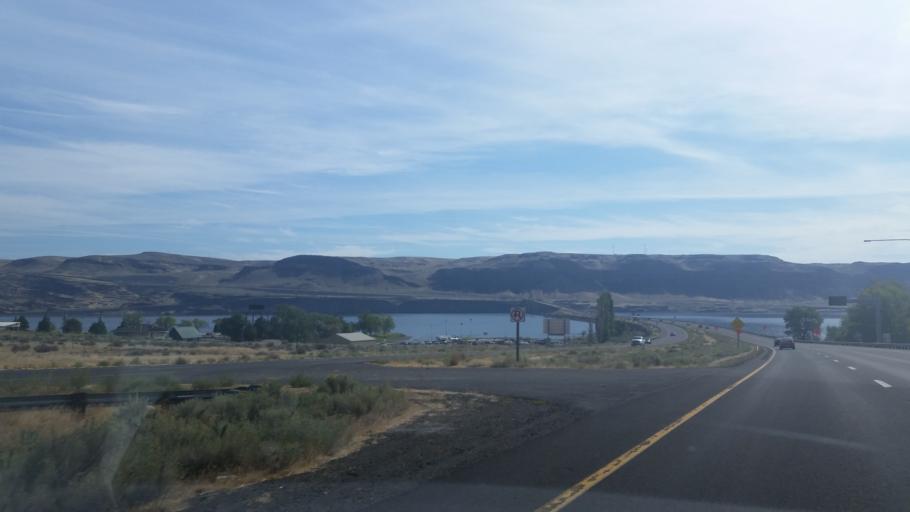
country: US
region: Washington
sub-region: Grant County
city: Mattawa
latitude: 46.9407
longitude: -119.9894
